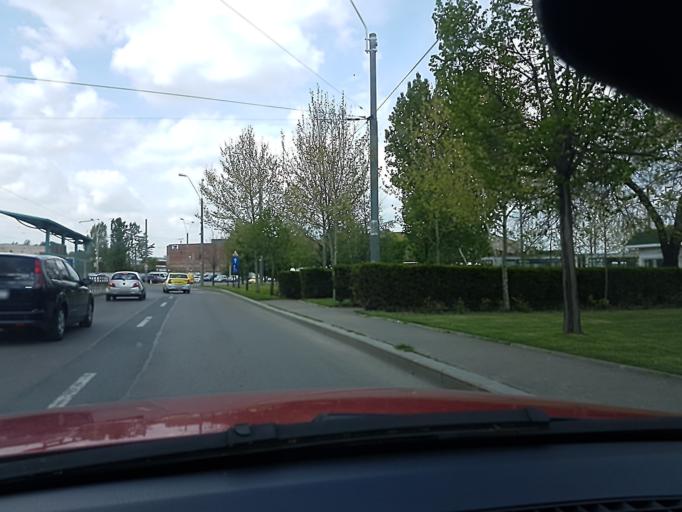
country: RO
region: Ilfov
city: Dobroesti
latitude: 44.4265
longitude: 26.1792
